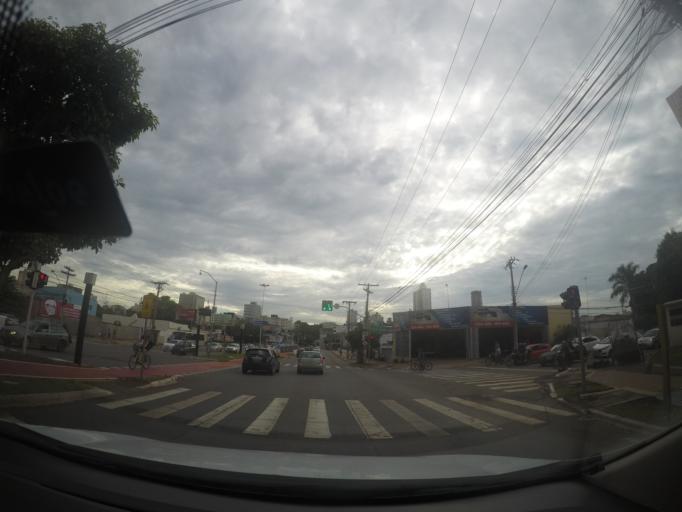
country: BR
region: Goias
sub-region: Goiania
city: Goiania
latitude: -16.6790
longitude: -49.2502
